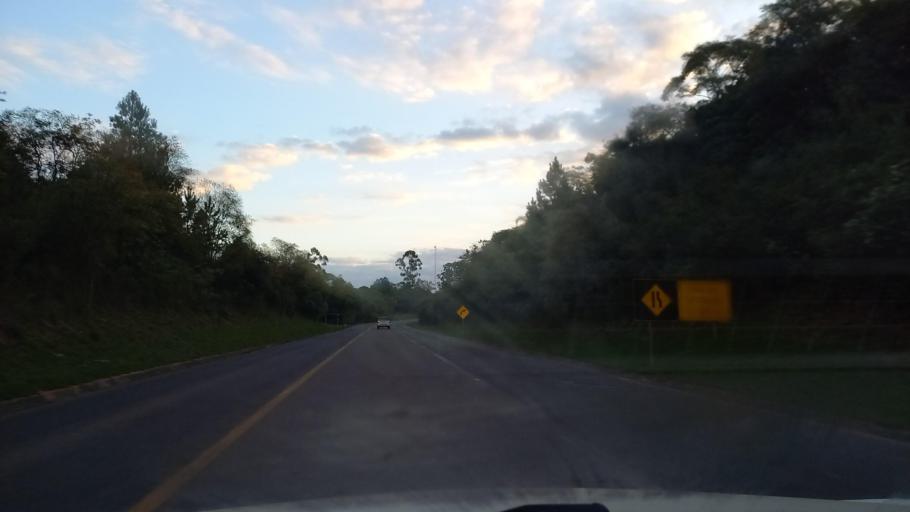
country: BR
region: Rio Grande do Sul
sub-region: Santa Cruz Do Sul
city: Santa Cruz do Sul
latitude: -29.6986
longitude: -52.5108
